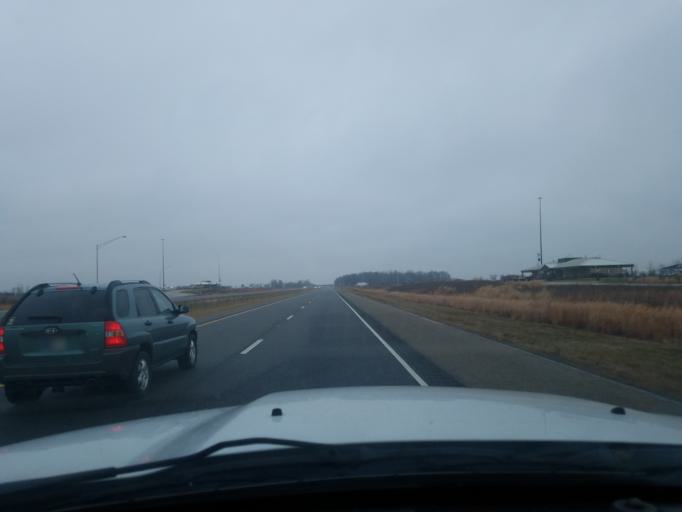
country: US
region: Indiana
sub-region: Grant County
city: Fairmount
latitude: 40.3526
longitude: -85.5586
